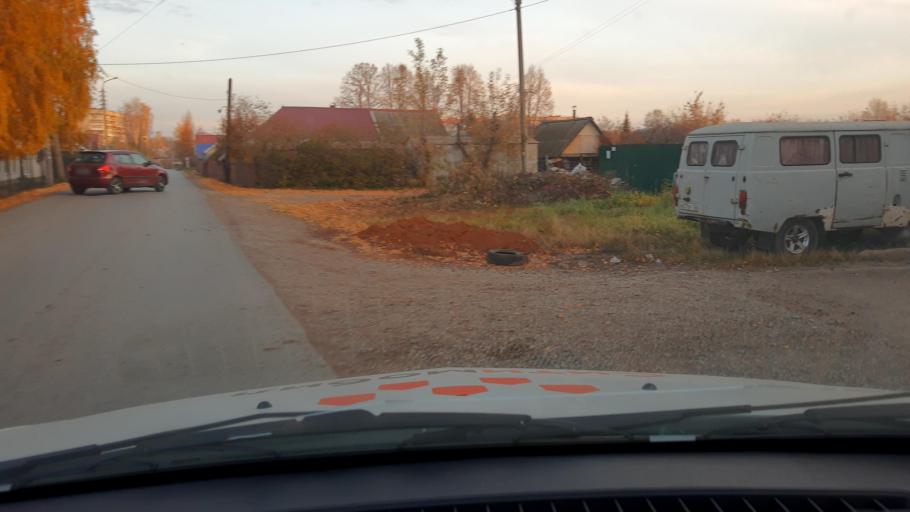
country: RU
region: Bashkortostan
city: Iglino
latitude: 54.7633
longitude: 56.2288
